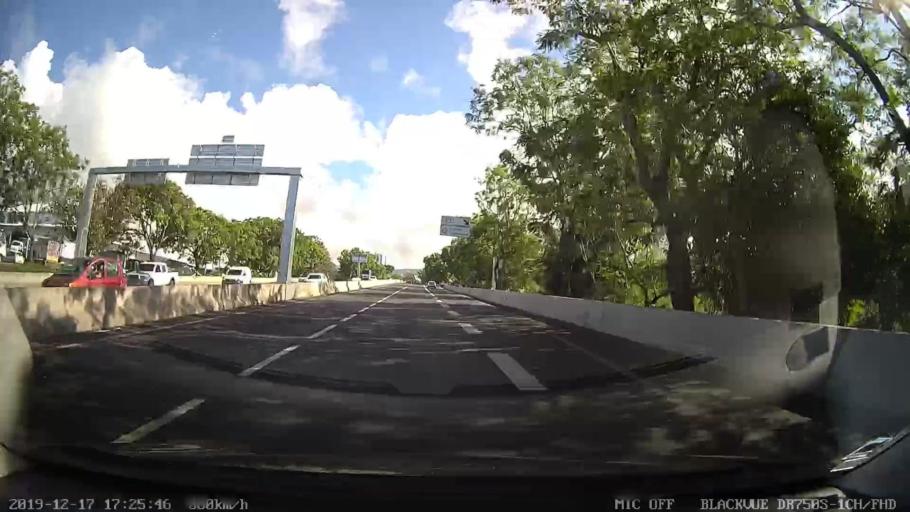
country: RE
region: Reunion
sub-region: Reunion
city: Le Tampon
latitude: -21.2913
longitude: 55.5136
